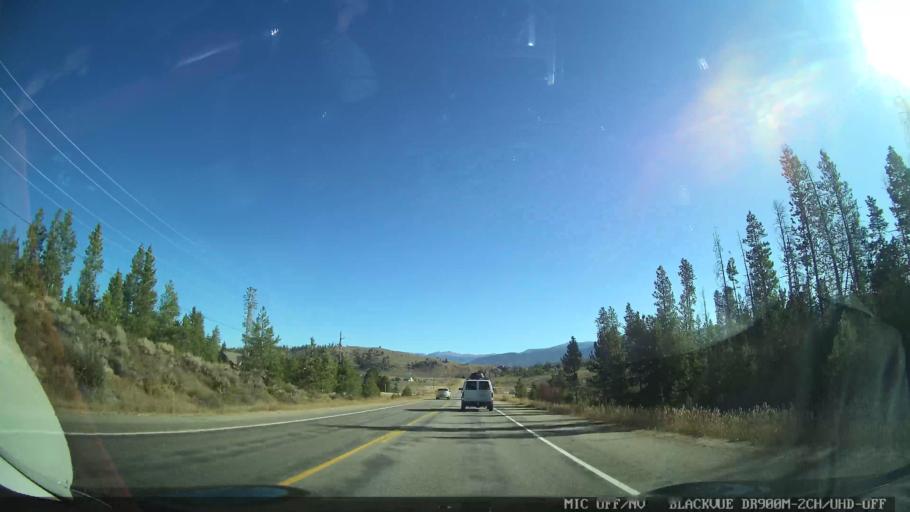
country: US
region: Colorado
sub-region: Grand County
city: Granby
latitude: 40.1776
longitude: -105.8969
